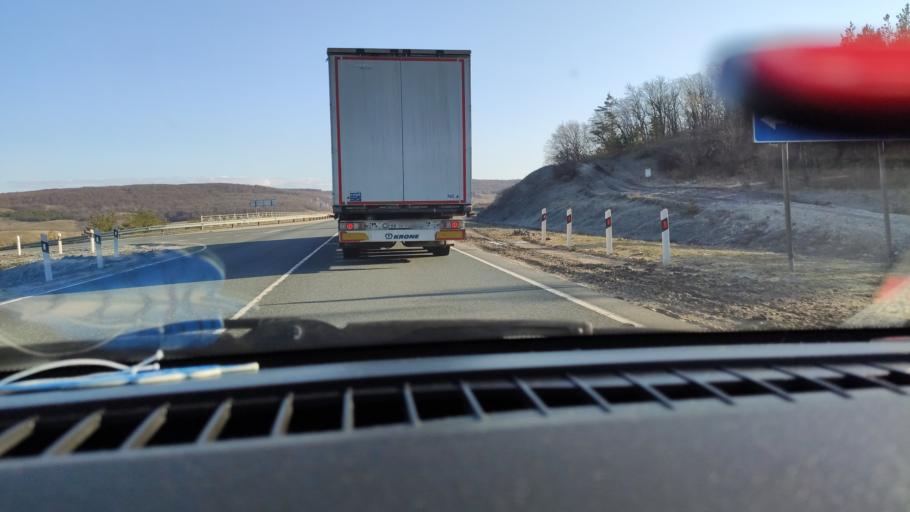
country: RU
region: Saratov
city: Alekseyevka
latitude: 52.3885
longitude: 47.9754
